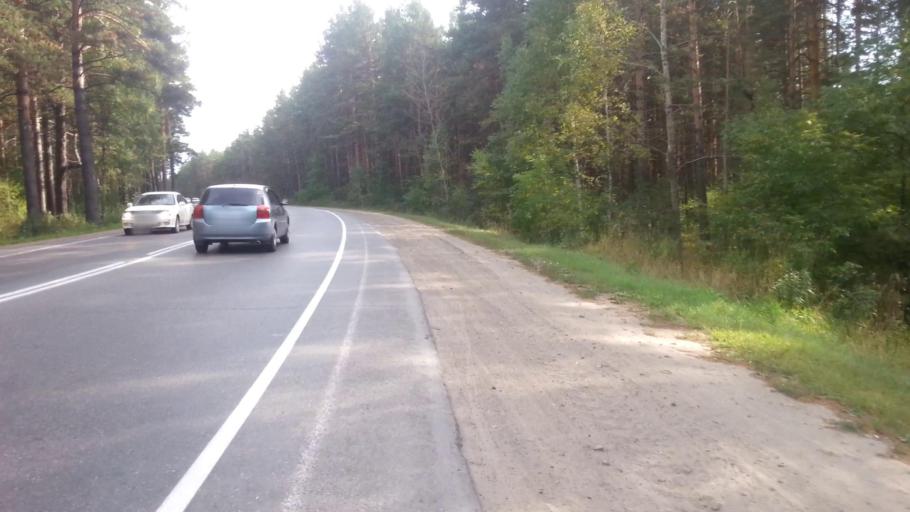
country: RU
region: Altai Krai
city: Yuzhnyy
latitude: 53.2986
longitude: 83.7028
